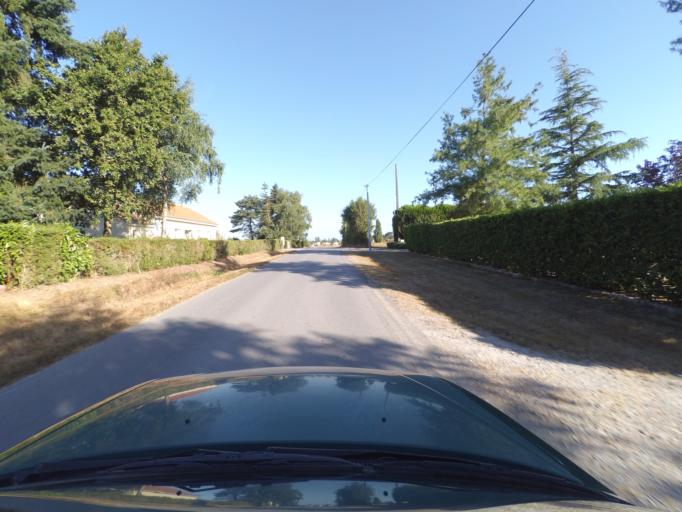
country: FR
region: Pays de la Loire
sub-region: Departement de la Loire-Atlantique
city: Le Bignon
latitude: 47.0935
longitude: -1.4827
